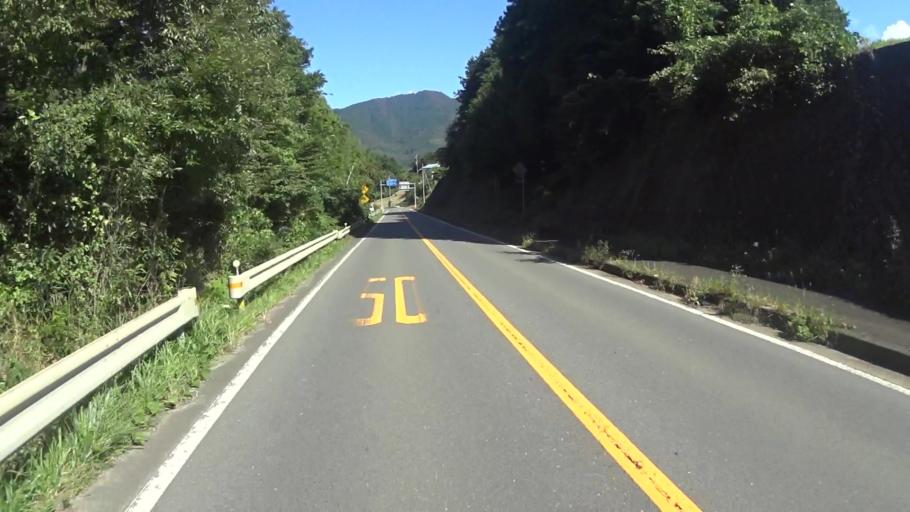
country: JP
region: Kyoto
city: Ayabe
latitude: 35.2502
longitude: 135.4177
